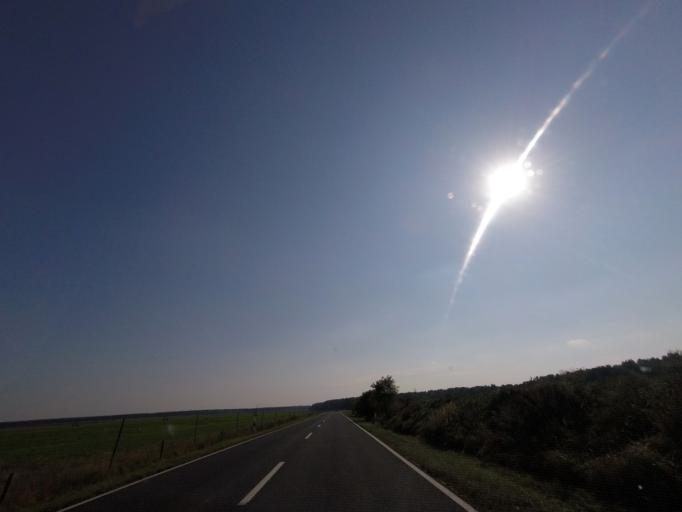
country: DE
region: Brandenburg
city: Niedergorsdorf
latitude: 51.8997
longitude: 13.0243
